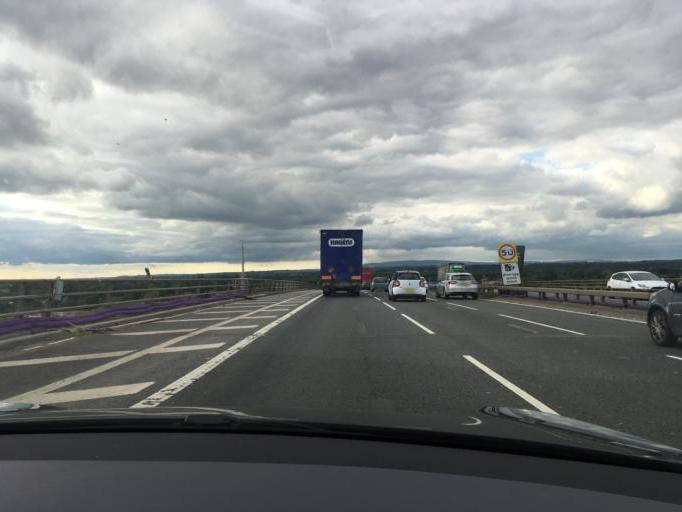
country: GB
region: England
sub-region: Trafford
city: Urmston
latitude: 53.4692
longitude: -2.3691
